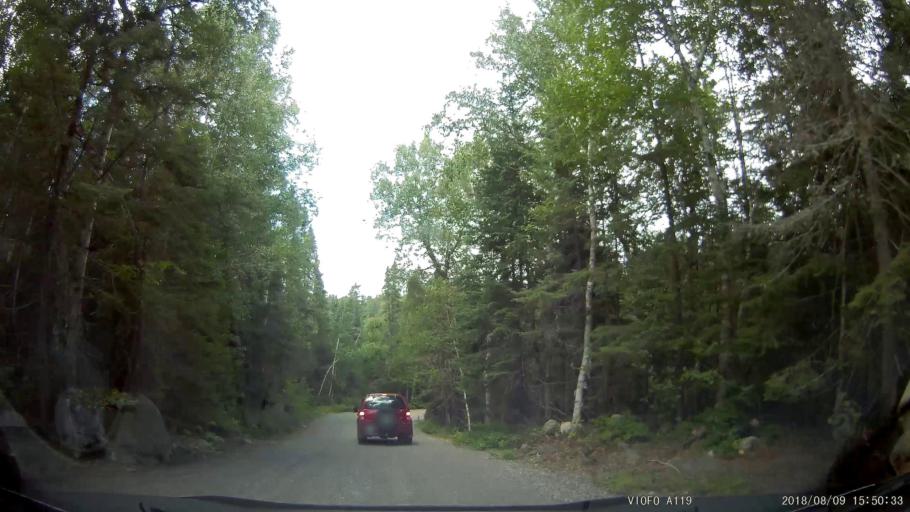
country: CA
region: Ontario
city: Rayside-Balfour
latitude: 46.5928
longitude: -81.5372
